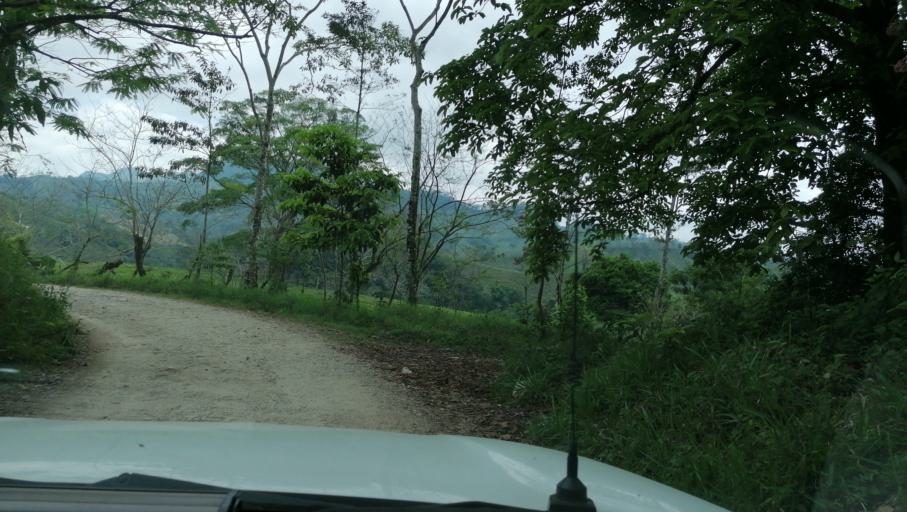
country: MX
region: Chiapas
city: Ocotepec
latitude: 17.2802
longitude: -93.2287
